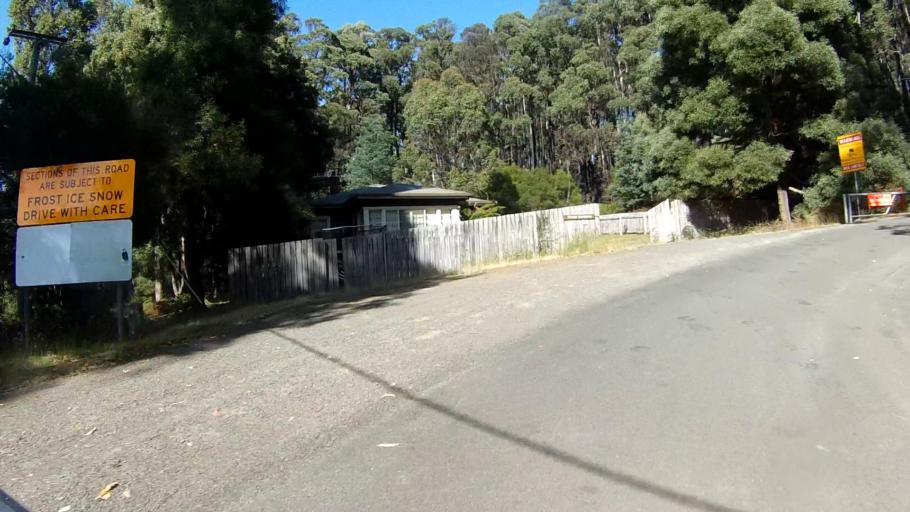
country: AU
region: Tasmania
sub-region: Derwent Valley
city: New Norfolk
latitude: -42.6833
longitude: 146.7156
